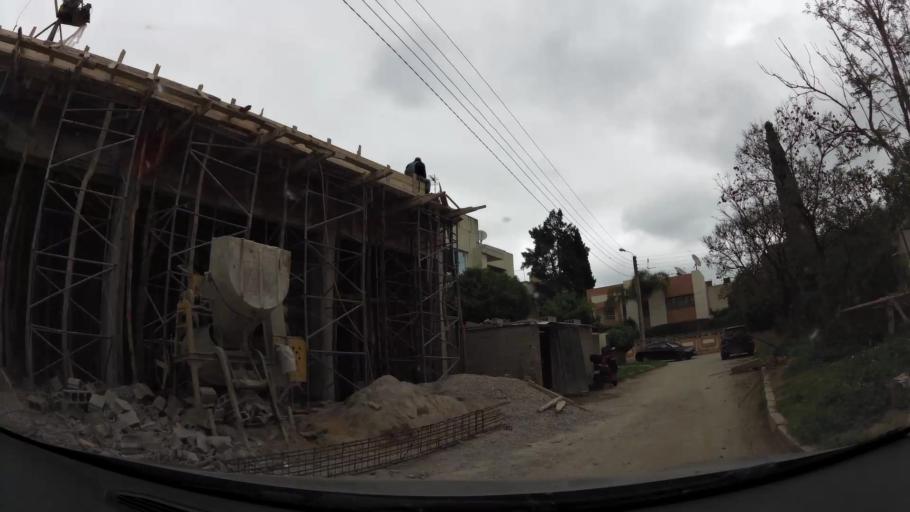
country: MA
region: Fes-Boulemane
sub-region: Fes
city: Fes
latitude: 34.0326
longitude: -5.0120
